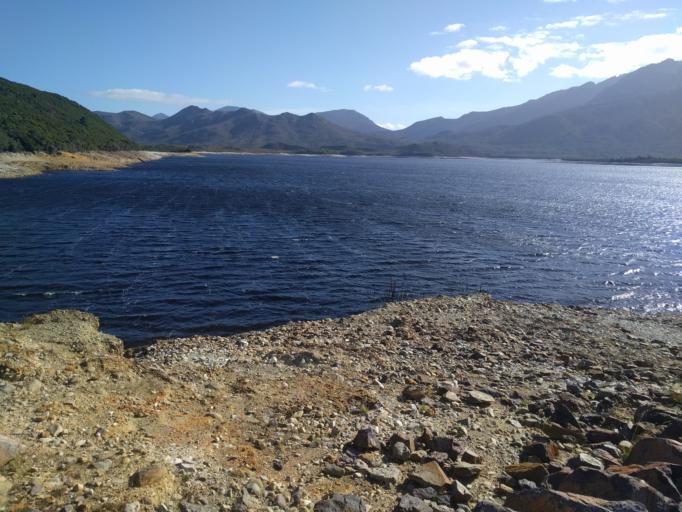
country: AU
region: Tasmania
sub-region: West Coast
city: Queenstown
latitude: -42.0963
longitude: 145.6733
